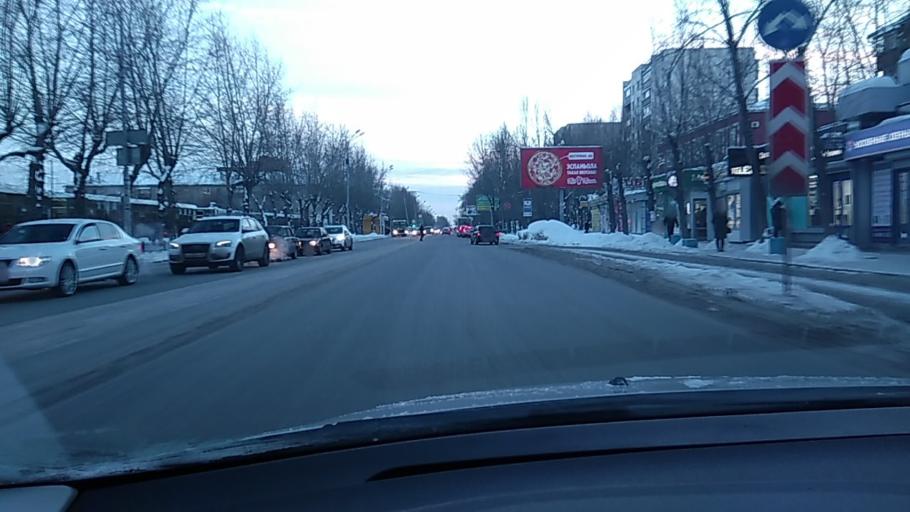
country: RU
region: Sverdlovsk
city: Yekaterinburg
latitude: 56.8305
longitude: 60.6361
